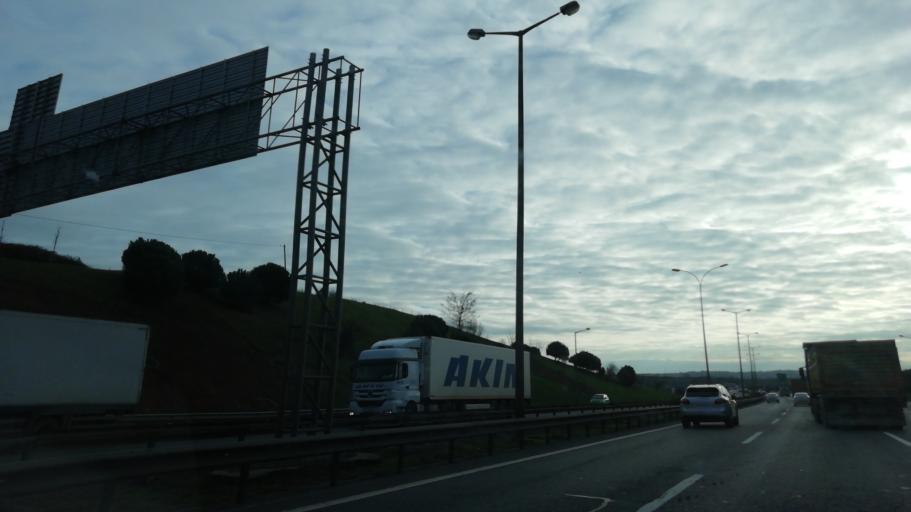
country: TR
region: Istanbul
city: Sultanbeyli
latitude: 40.9357
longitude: 29.3330
